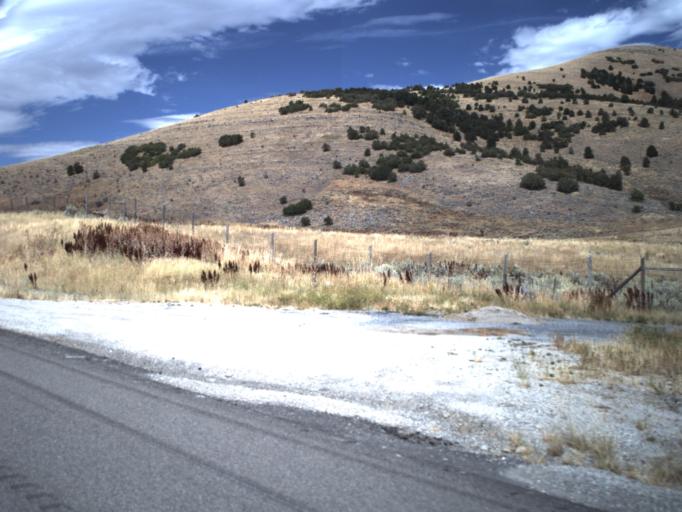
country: US
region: Utah
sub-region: Cache County
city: Wellsville
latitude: 41.5730
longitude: -111.9698
